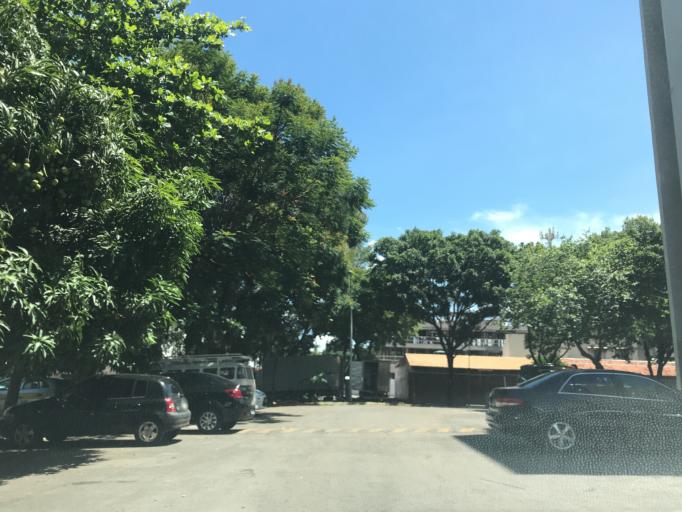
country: BR
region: Federal District
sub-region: Brasilia
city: Brasilia
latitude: -15.7762
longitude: -47.8892
